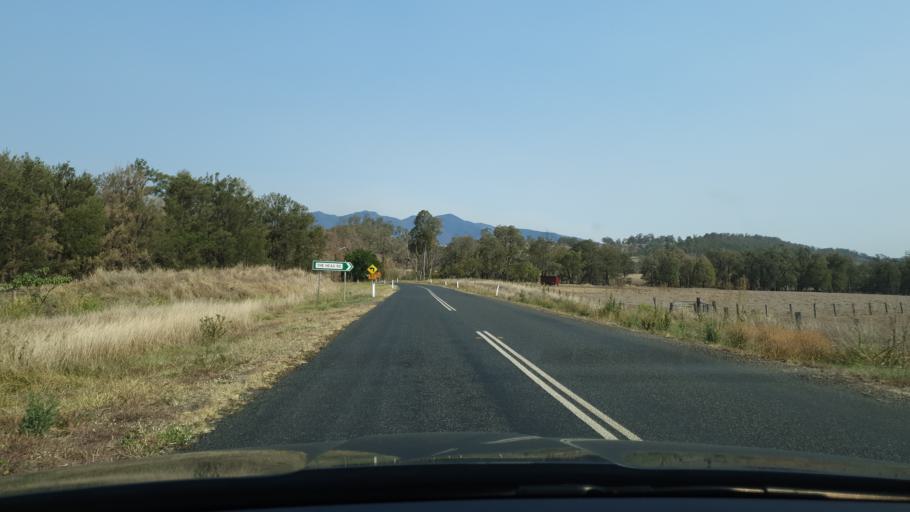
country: AU
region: Queensland
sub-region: Southern Downs
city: Warwick
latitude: -28.1811
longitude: 152.5435
